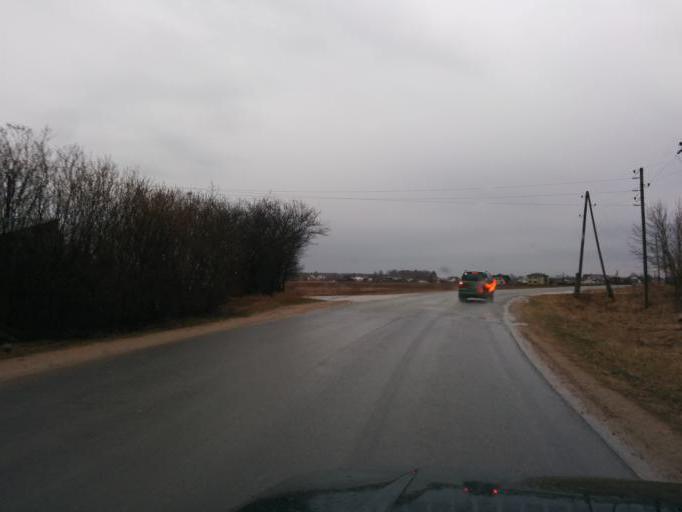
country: LV
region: Kekava
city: Balozi
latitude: 56.8946
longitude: 24.1753
